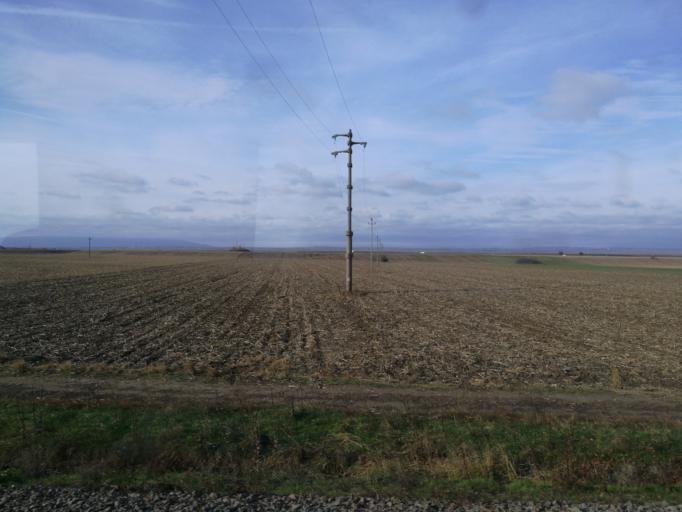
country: RO
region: Vrancea
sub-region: Comuna Pufesti
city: Ciorani
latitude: 45.9364
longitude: 27.2157
